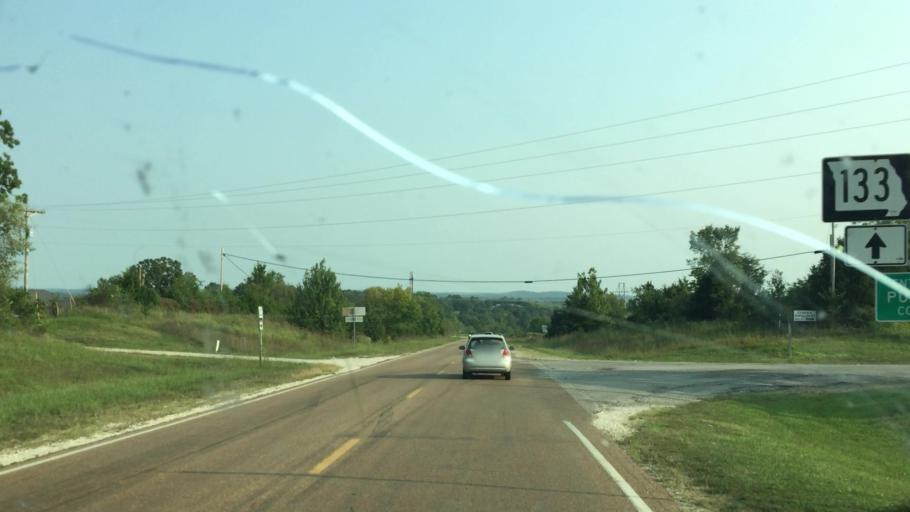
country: US
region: Missouri
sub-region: Pulaski County
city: Richland
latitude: 37.8418
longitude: -92.4097
